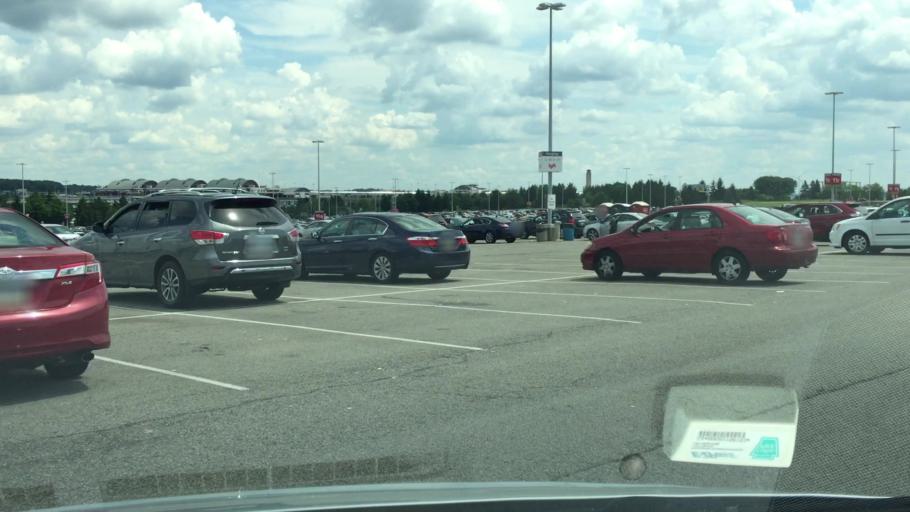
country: US
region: Pennsylvania
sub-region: Allegheny County
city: Imperial
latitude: 40.4912
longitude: -80.2644
